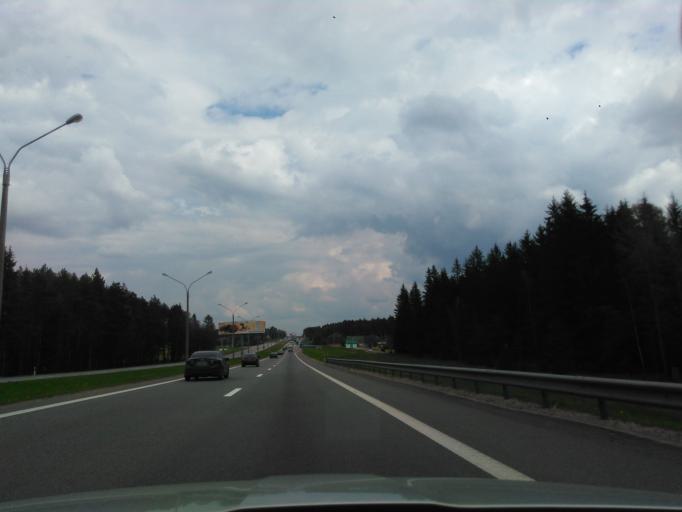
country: BY
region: Minsk
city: Kalodzishchy
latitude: 53.9736
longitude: 27.7606
